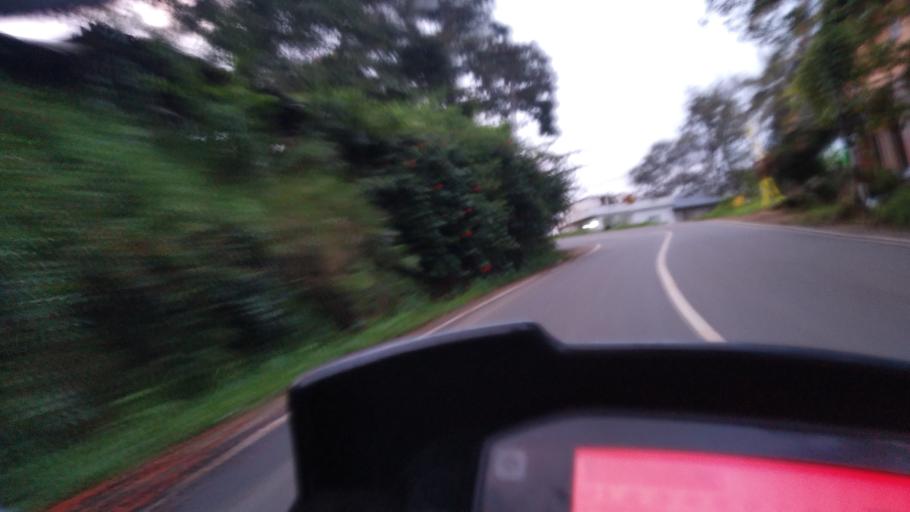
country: IN
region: Kerala
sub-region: Idukki
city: Munnar
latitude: 9.9685
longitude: 77.1192
